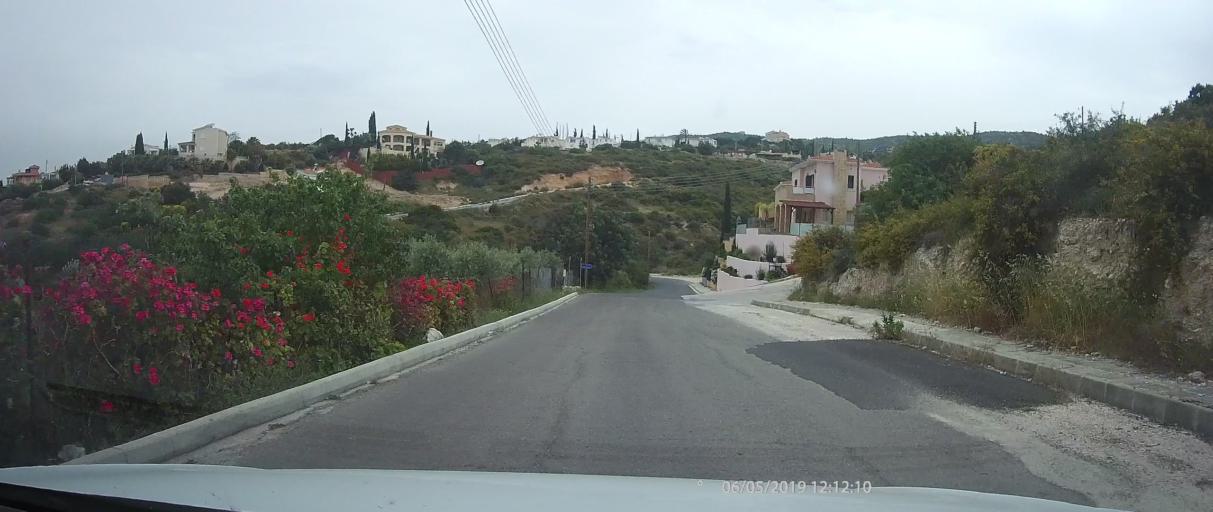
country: CY
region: Pafos
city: Tala
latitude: 34.8405
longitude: 32.4284
